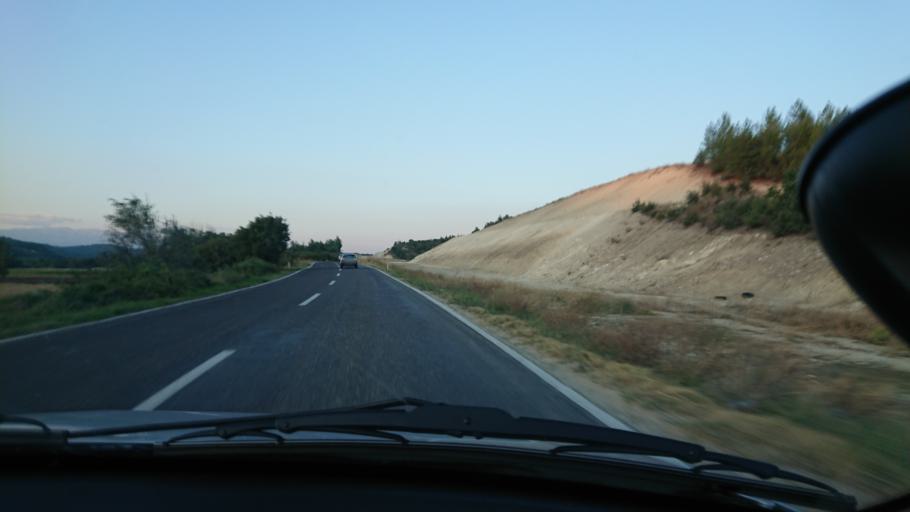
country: TR
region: Usak
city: Gure
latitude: 38.7859
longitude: 29.2259
